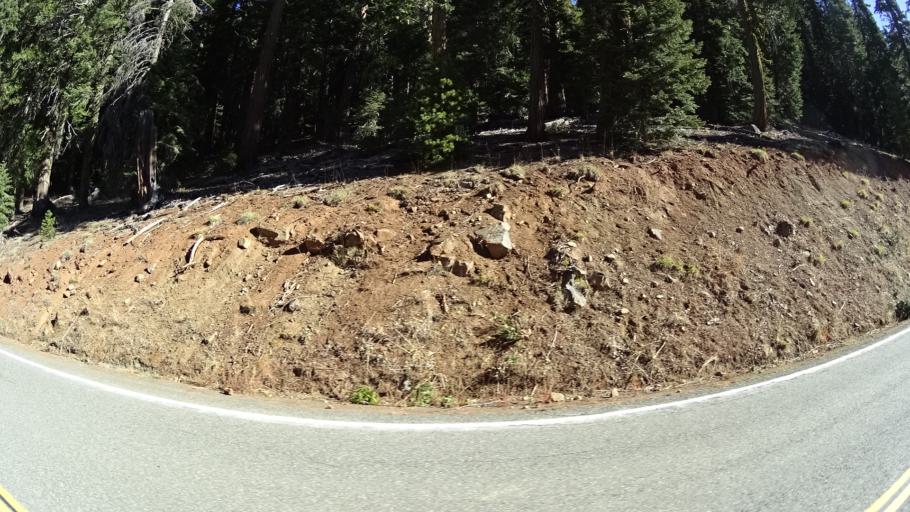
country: US
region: California
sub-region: Trinity County
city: Weaverville
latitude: 41.2255
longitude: -122.9234
